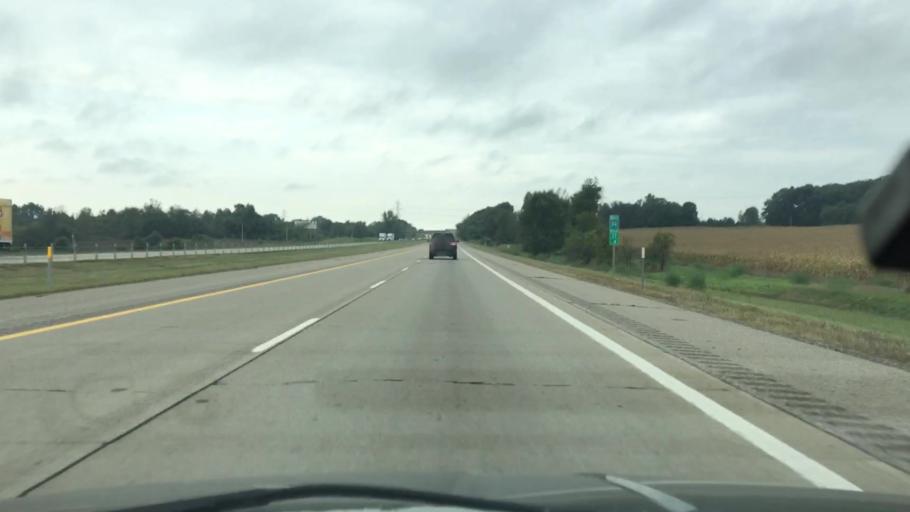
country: US
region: Michigan
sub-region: Berrien County
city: Coloma
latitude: 42.1676
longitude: -86.3237
